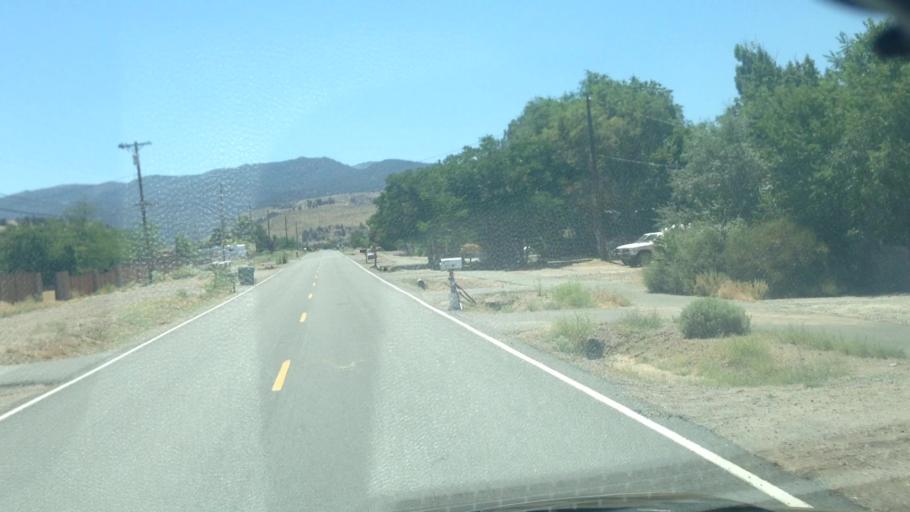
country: US
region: Nevada
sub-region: Storey County
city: Virginia City
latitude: 39.3813
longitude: -119.7215
